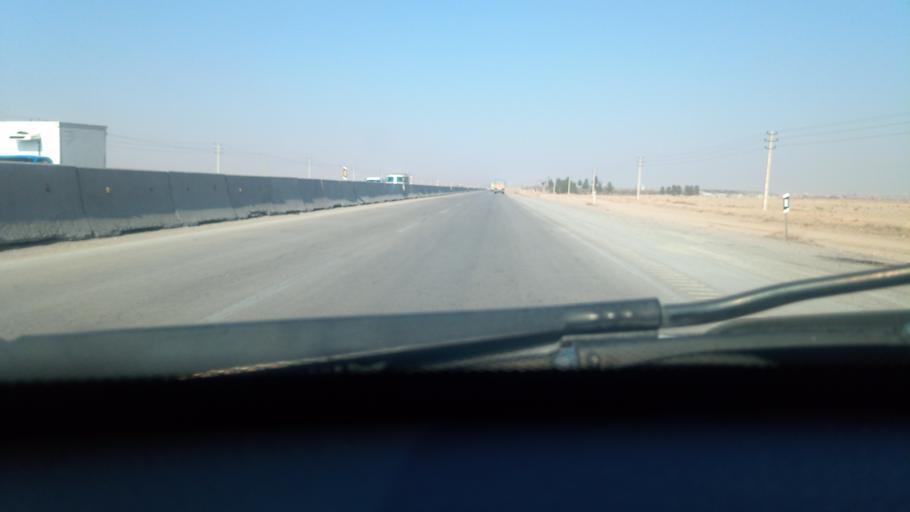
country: IR
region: Razavi Khorasan
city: Quchan
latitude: 36.8850
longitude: 58.7410
